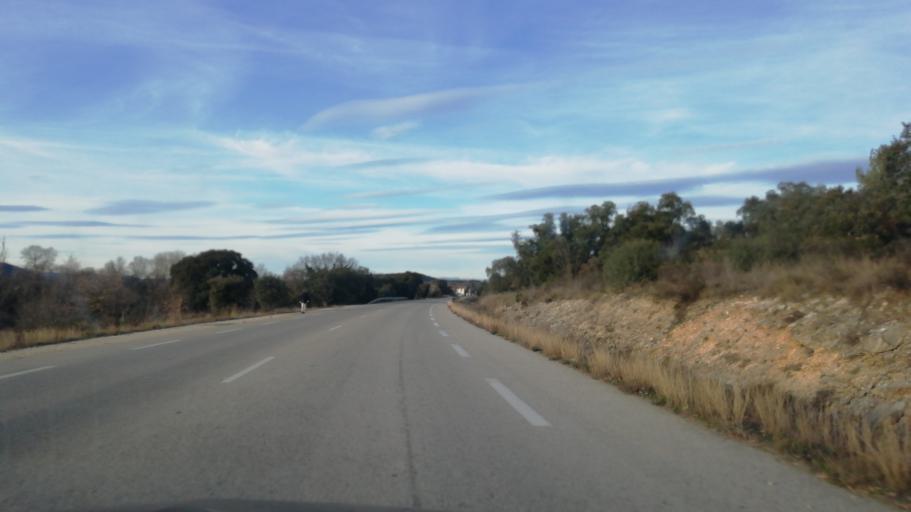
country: FR
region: Languedoc-Roussillon
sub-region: Departement du Gard
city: Quissac
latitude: 43.8977
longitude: 4.0074
